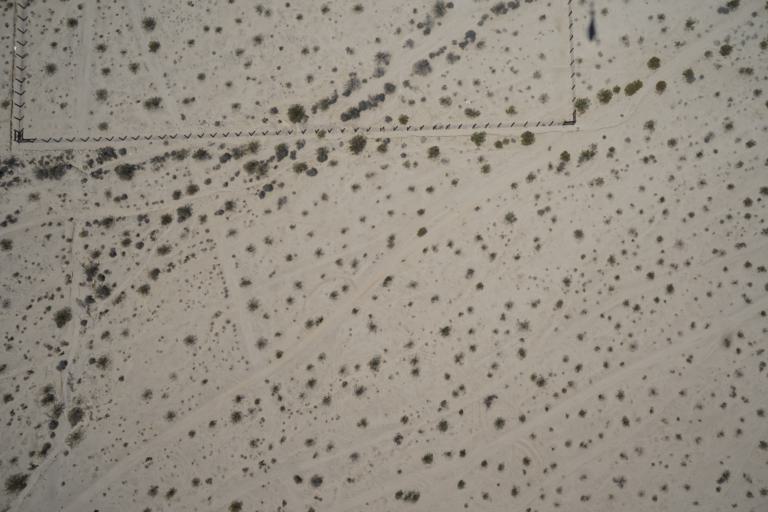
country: US
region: California
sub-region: San Bernardino County
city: Twentynine Palms
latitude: 34.1300
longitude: -116.0347
